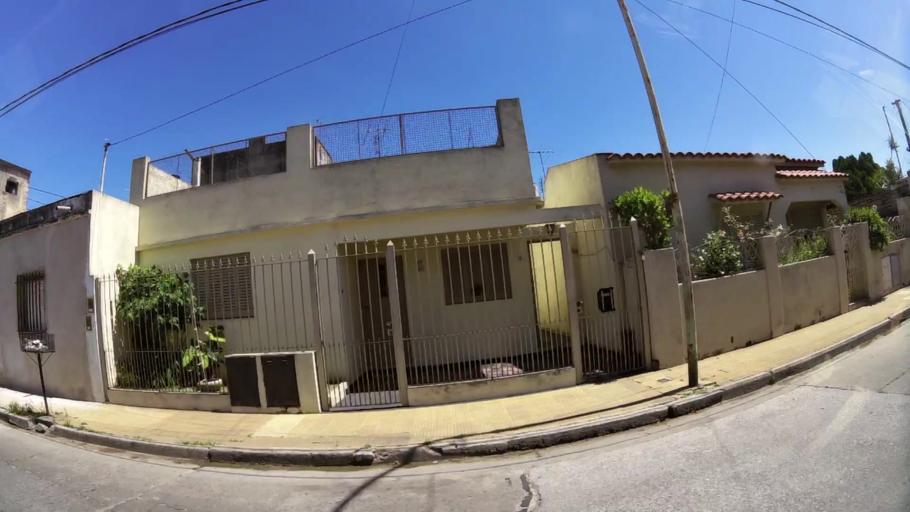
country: AR
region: Buenos Aires
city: Caseros
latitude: -34.5843
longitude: -58.5658
